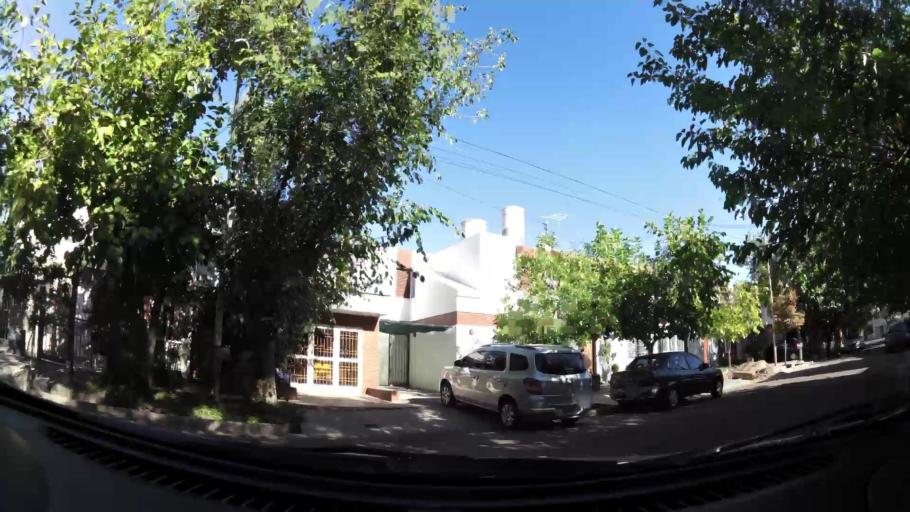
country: AR
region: Mendoza
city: Villa Nueva
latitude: -32.9054
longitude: -68.7965
